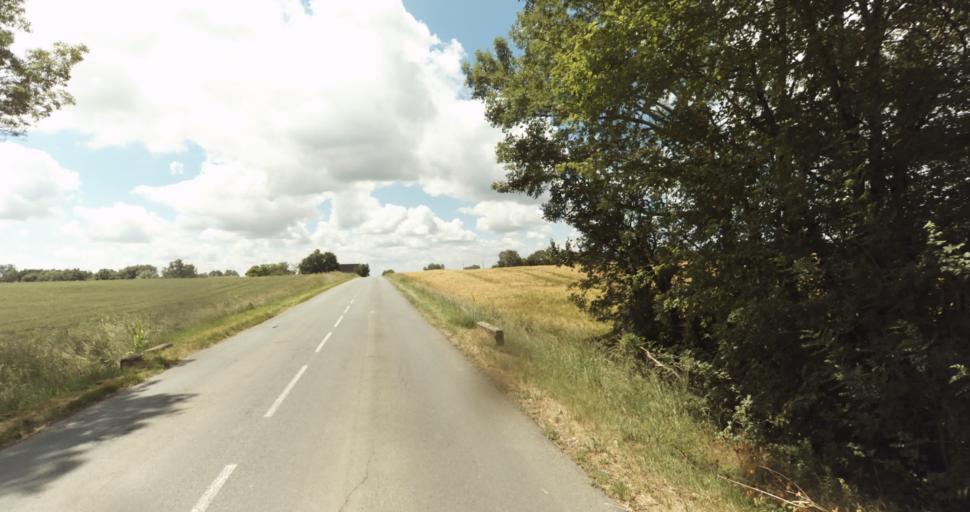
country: FR
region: Aquitaine
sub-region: Departement de la Dordogne
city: Beaumont-du-Perigord
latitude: 44.7205
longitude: 0.7548
